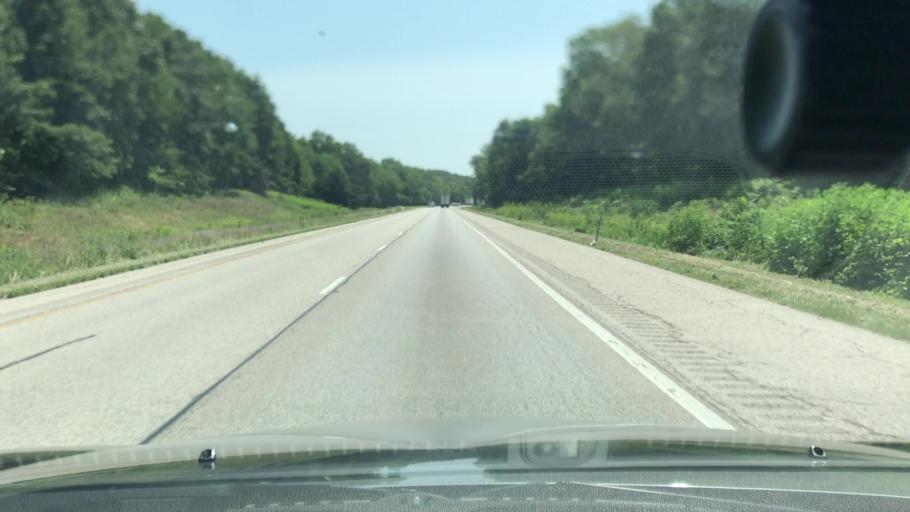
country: US
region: Illinois
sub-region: Washington County
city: Nashville
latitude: 38.4084
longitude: -89.4169
